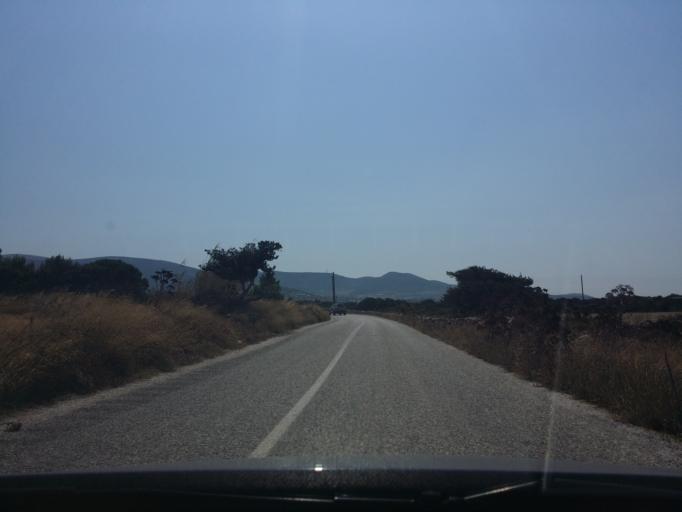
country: GR
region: South Aegean
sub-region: Nomos Kykladon
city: Antiparos
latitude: 37.0091
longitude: 25.1175
